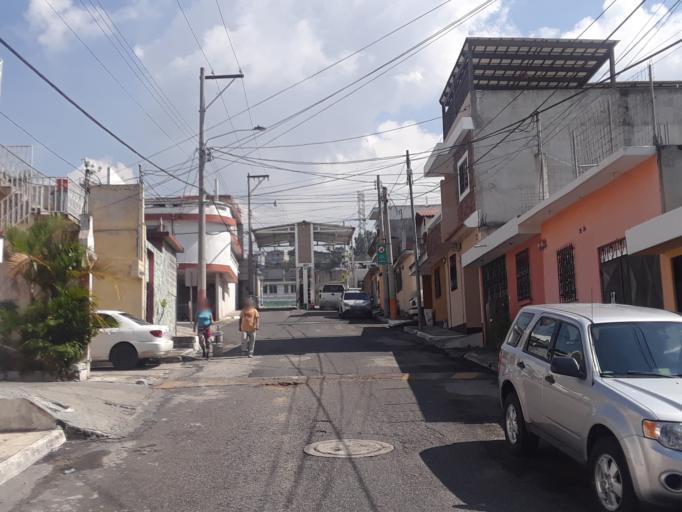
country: GT
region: Guatemala
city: Petapa
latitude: 14.5360
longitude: -90.5520
